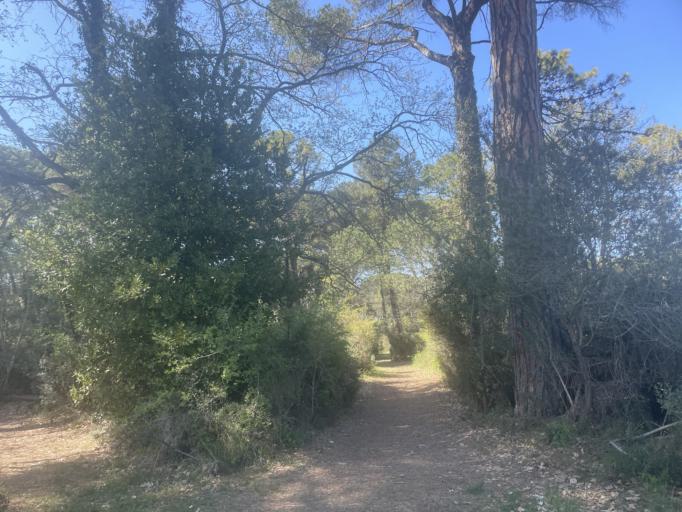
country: IT
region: Emilia-Romagna
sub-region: Provincia di Ravenna
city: Cervia
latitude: 44.2708
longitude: 12.3318
